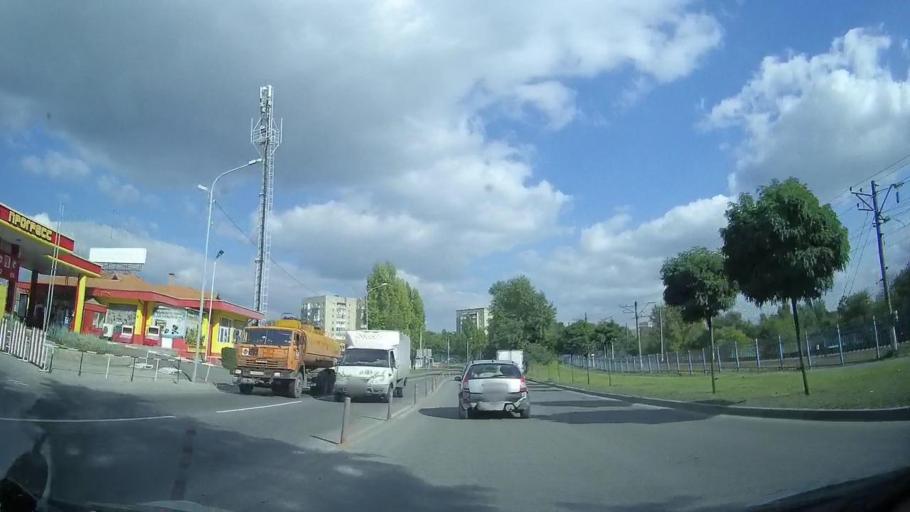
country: RU
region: Rostov
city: Imeni Chkalova
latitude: 47.2625
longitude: 39.7739
